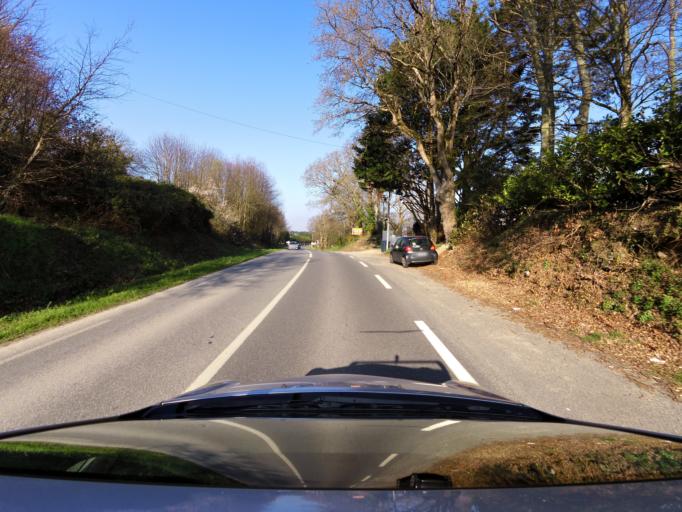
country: FR
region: Brittany
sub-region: Departement du Morbihan
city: Ploemeur
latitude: 47.7386
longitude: -3.4469
